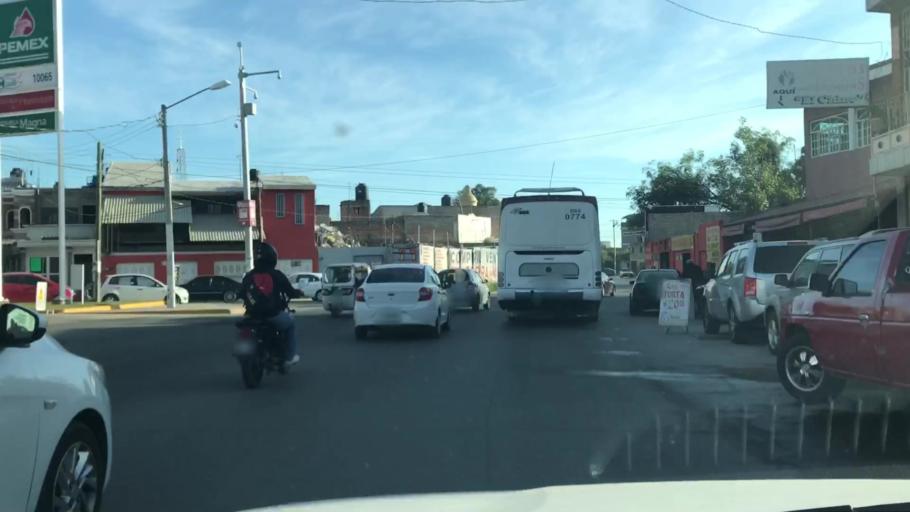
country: MX
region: Jalisco
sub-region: Tlajomulco de Zuniga
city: Palomar
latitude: 20.6484
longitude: -103.4580
